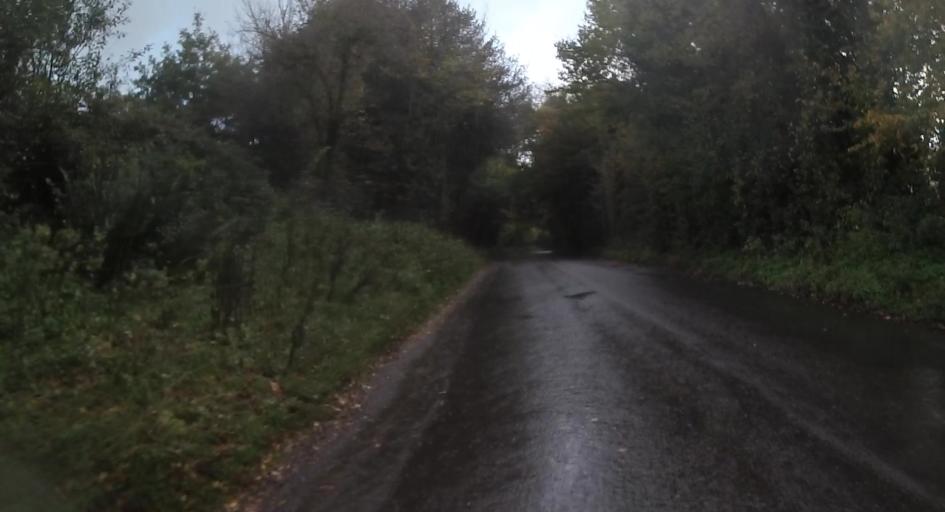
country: GB
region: England
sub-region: Hampshire
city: Long Sutton
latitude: 51.1980
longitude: -0.9258
